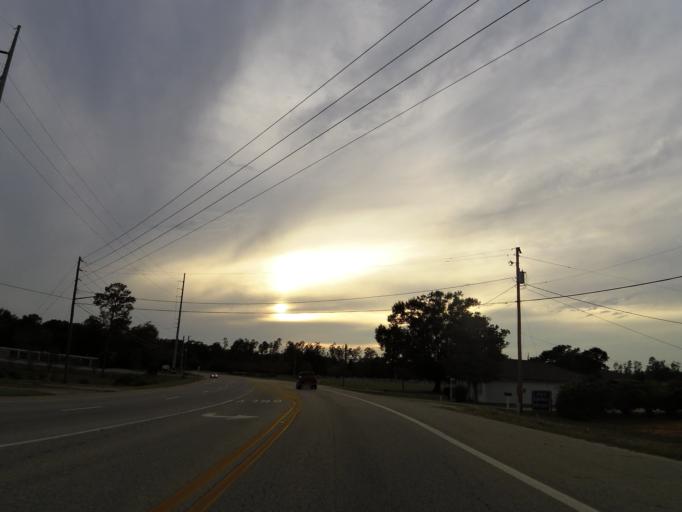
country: US
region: Alabama
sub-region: Baldwin County
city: Bay Minette
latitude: 30.8903
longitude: -87.7593
